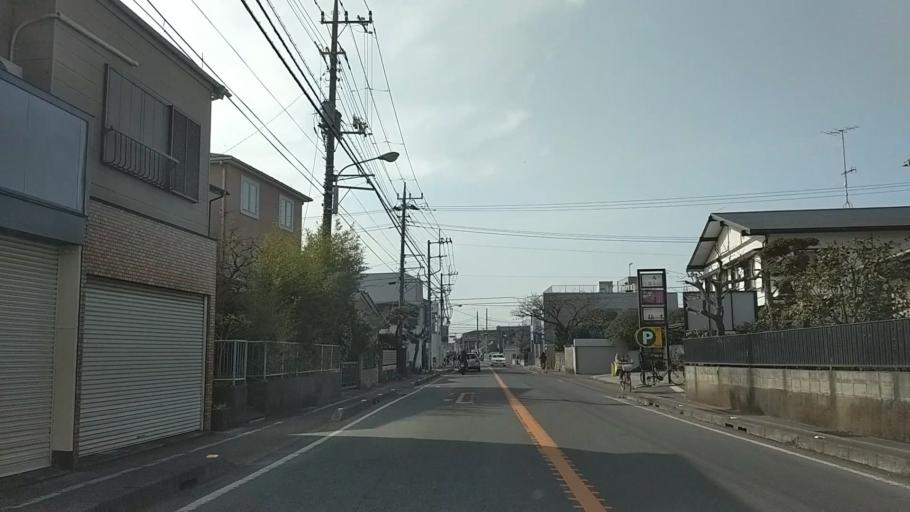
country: JP
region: Kanagawa
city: Chigasaki
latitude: 35.3330
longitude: 139.4233
